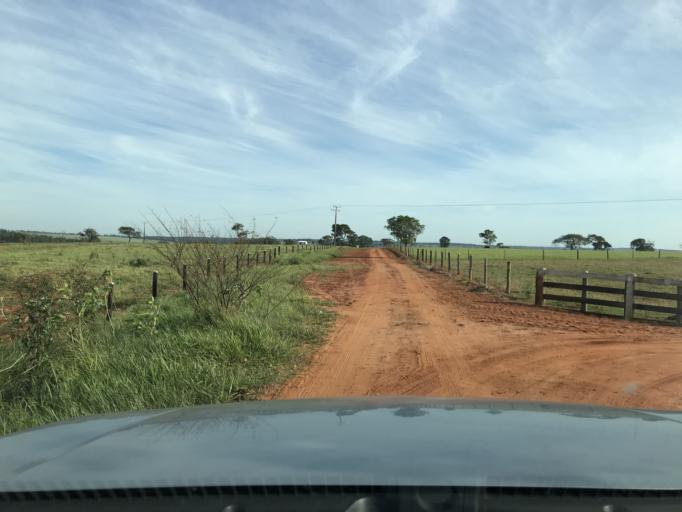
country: BR
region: Mato Grosso do Sul
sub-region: Iguatemi
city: Iguatemi
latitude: -23.6566
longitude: -54.5712
